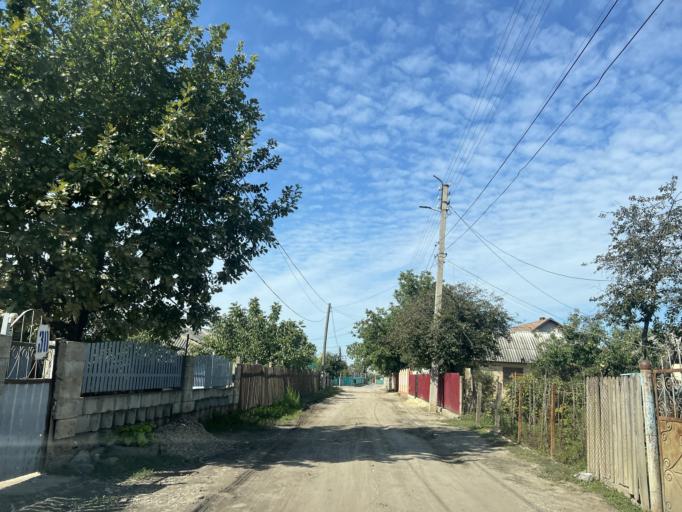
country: MD
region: Ungheni
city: Ungheni
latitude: 47.1999
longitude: 27.8155
